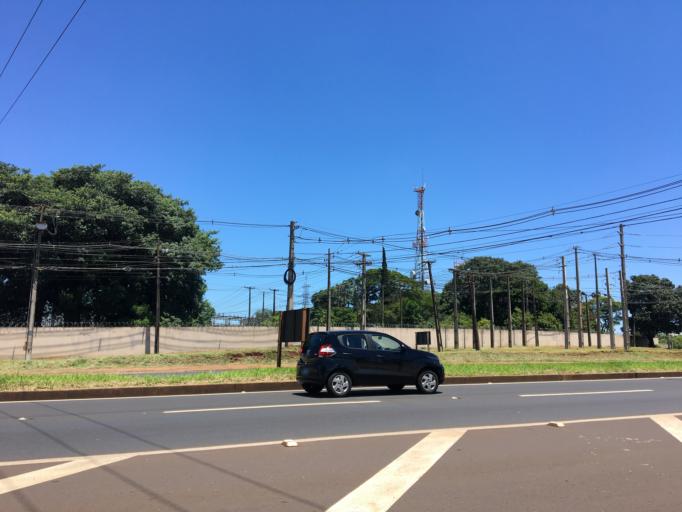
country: BR
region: Parana
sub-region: Maringa
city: Maringa
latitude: -23.4488
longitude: -51.9854
